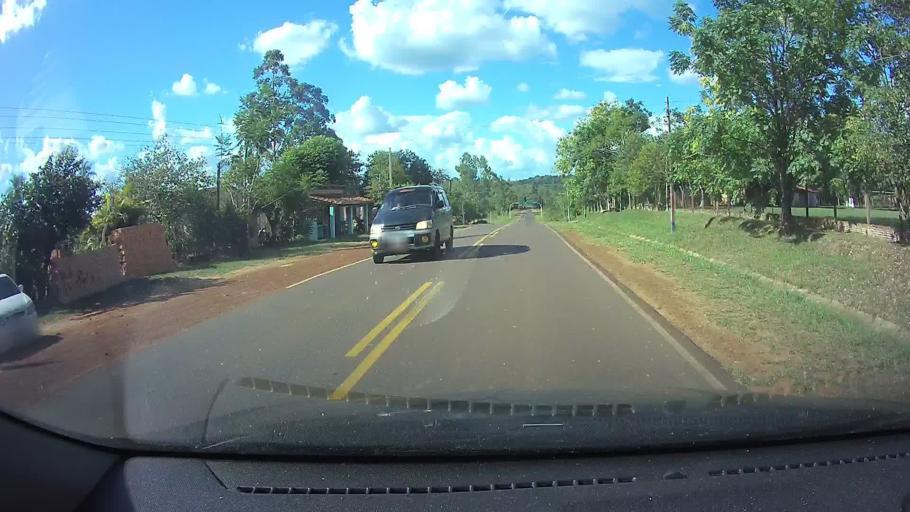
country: PY
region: Cordillera
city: Itacurubi de la Cordillera
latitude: -25.4687
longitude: -56.8795
